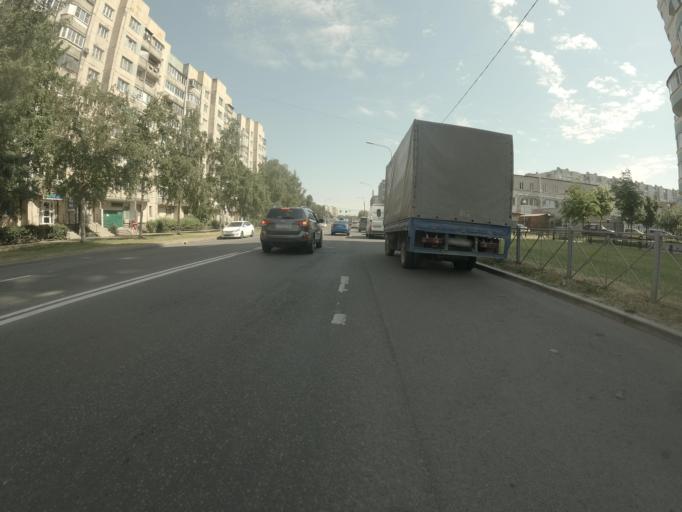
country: RU
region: St.-Petersburg
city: Krasnogvargeisky
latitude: 59.9534
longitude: 30.4800
